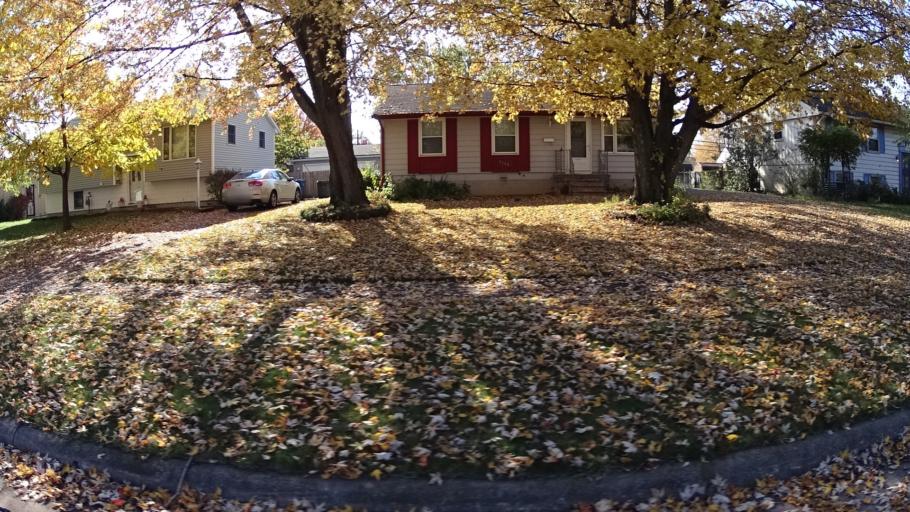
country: US
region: Ohio
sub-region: Lorain County
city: Lorain
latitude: 41.4696
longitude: -82.1482
